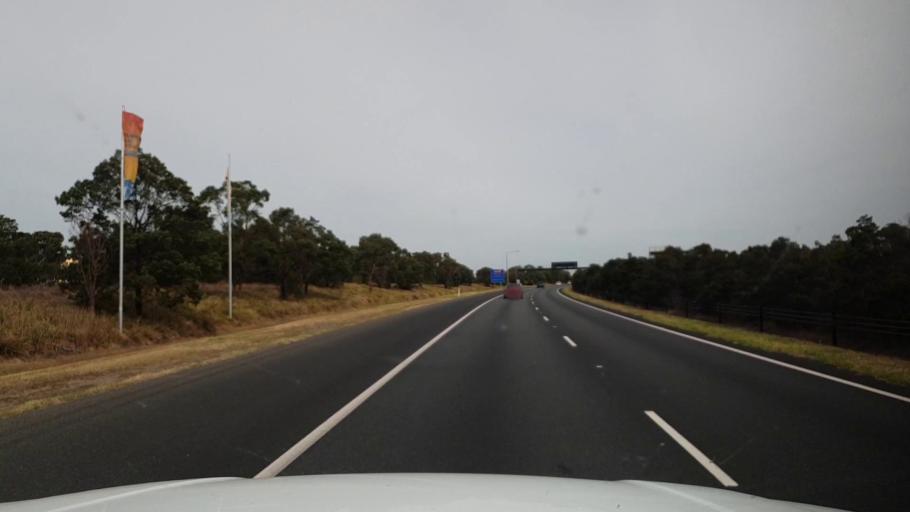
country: AU
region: Victoria
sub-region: Frankston
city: Carrum Downs
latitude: -38.0818
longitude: 145.1774
